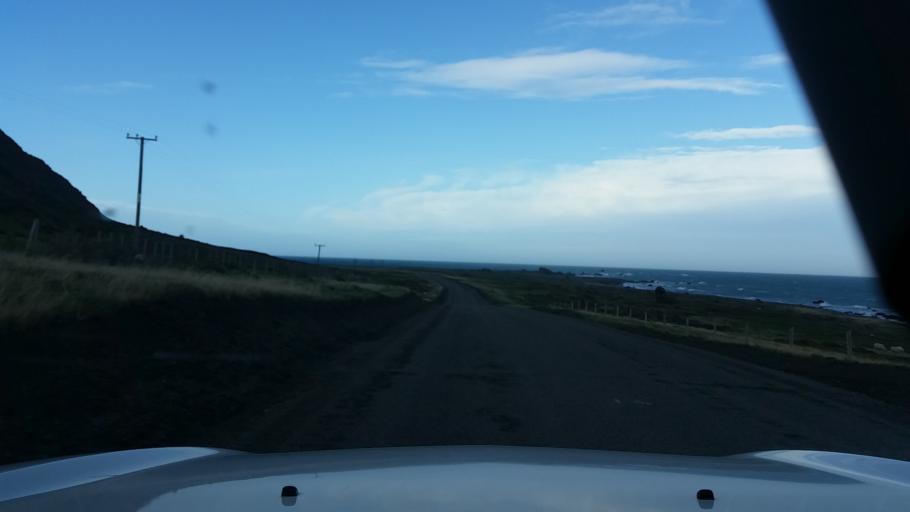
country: NZ
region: Wellington
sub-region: South Wairarapa District
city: Waipawa
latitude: -41.5956
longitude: 175.2344
